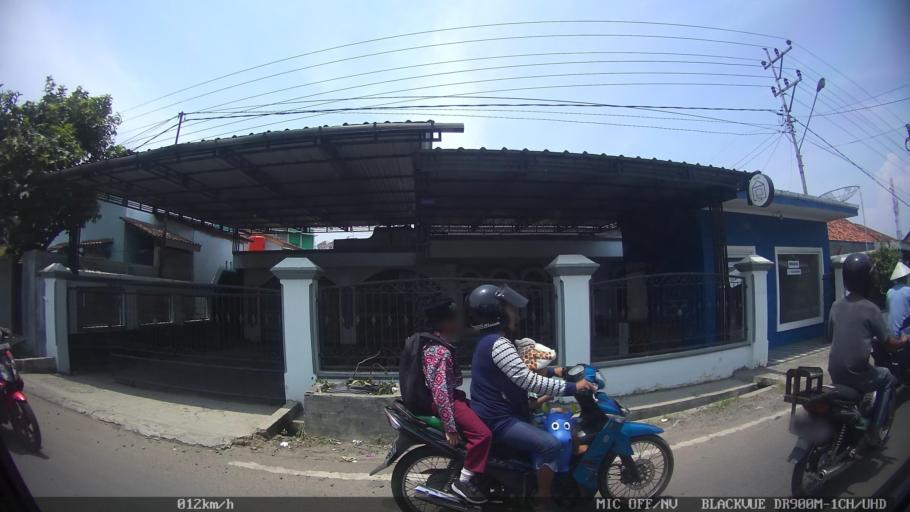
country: ID
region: Lampung
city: Bandarlampung
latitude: -5.4456
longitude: 105.2551
